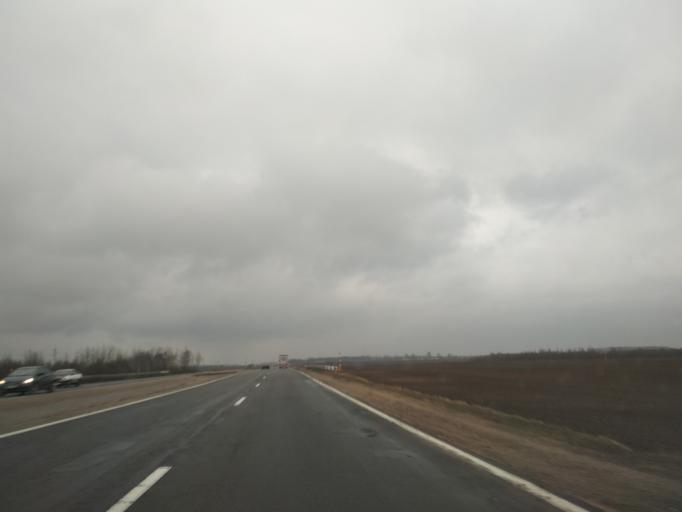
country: BY
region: Minsk
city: Dukora
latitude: 53.6462
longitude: 27.9830
